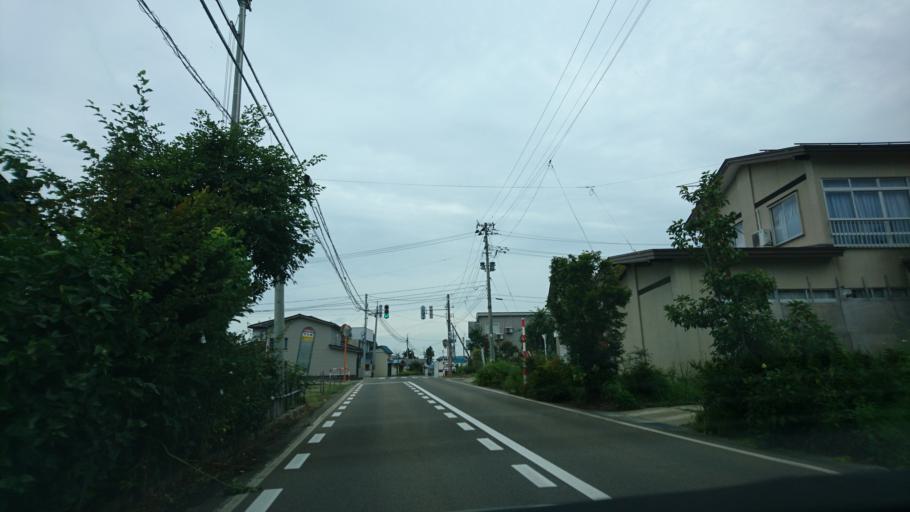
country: JP
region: Akita
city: Yuzawa
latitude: 39.1436
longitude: 140.5760
